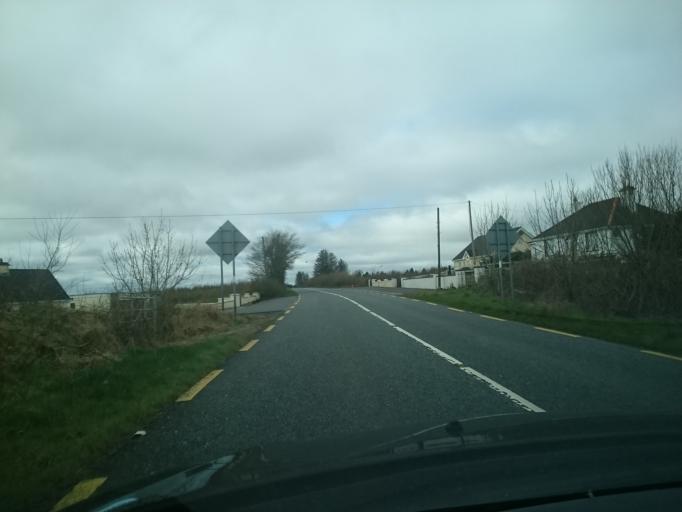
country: IE
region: Connaught
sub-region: Maigh Eo
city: Claremorris
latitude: 53.7173
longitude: -8.8904
